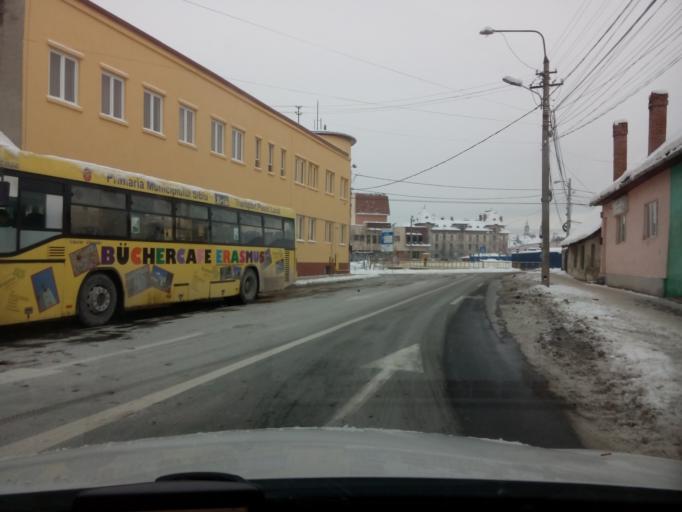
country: RO
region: Sibiu
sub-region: Municipiul Sibiu
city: Sibiu
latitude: 45.8009
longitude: 24.1437
